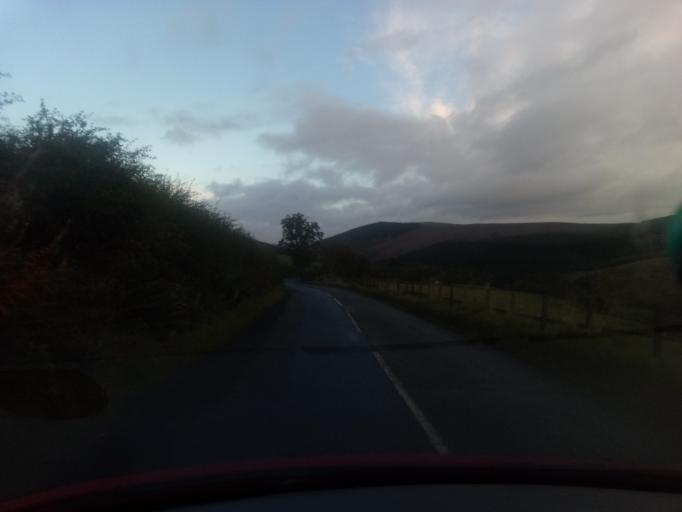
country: GB
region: Scotland
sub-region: The Scottish Borders
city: Hawick
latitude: 55.3412
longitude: -2.6516
